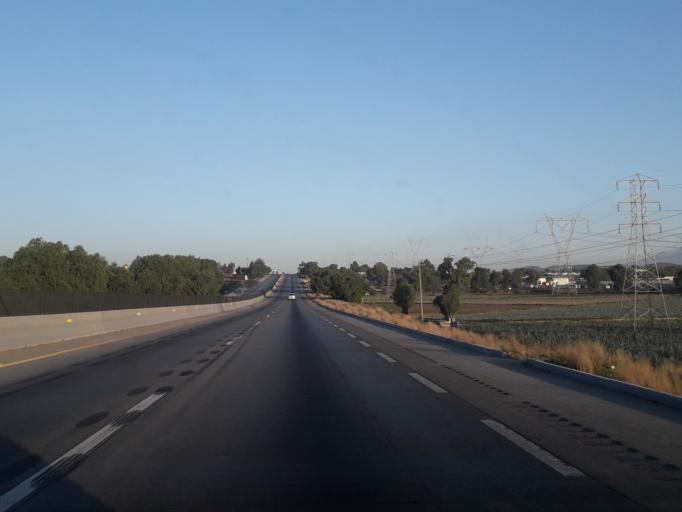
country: MX
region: Puebla
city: Actipan
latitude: 18.9739
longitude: -97.8016
